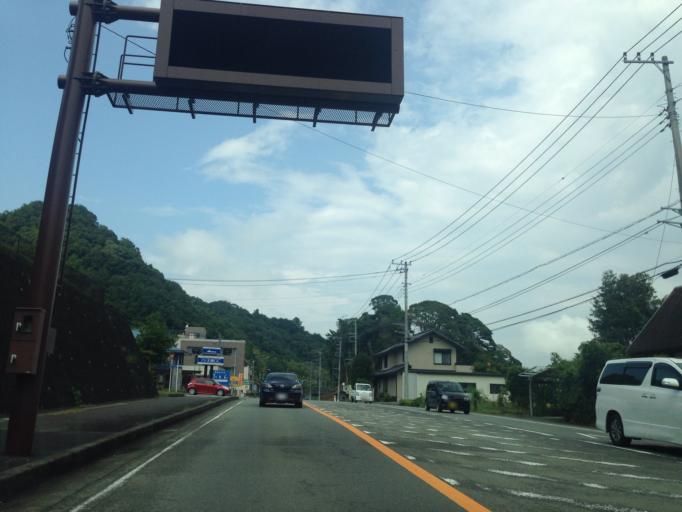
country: JP
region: Shizuoka
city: Heda
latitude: 34.9415
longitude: 138.9310
